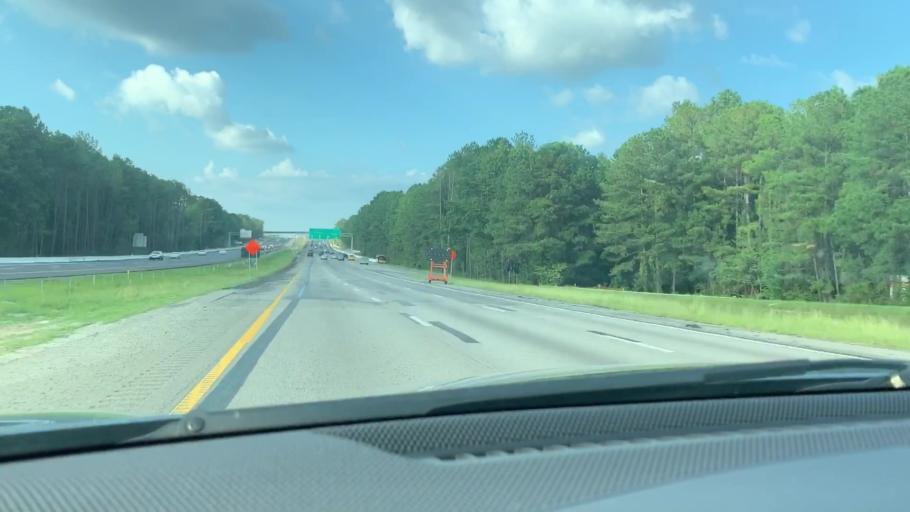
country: US
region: South Carolina
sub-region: Richland County
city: Woodfield
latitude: 34.0545
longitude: -80.9227
